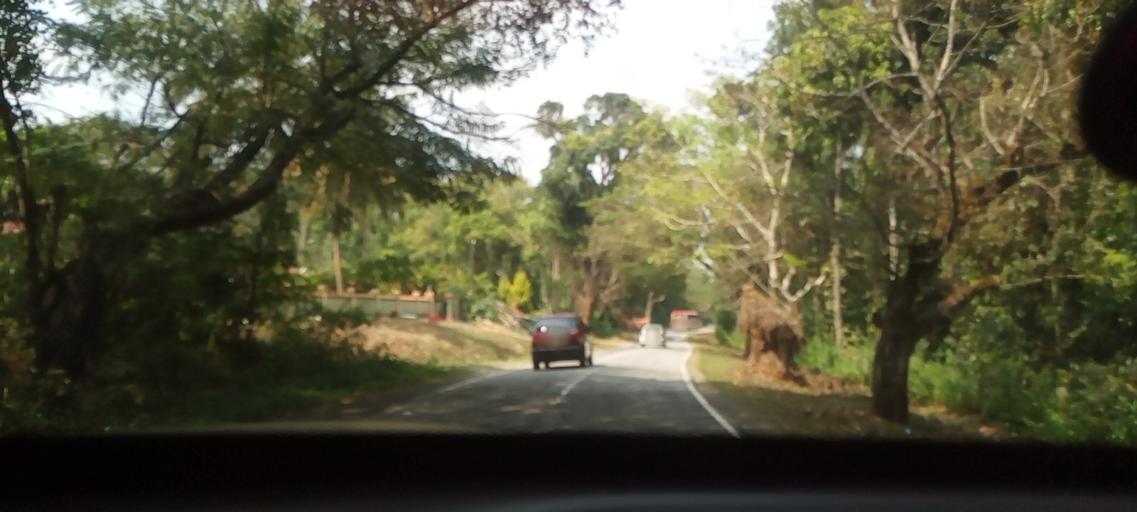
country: IN
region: Karnataka
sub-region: Chikmagalur
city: Chikmagalur
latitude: 13.2596
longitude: 75.6699
